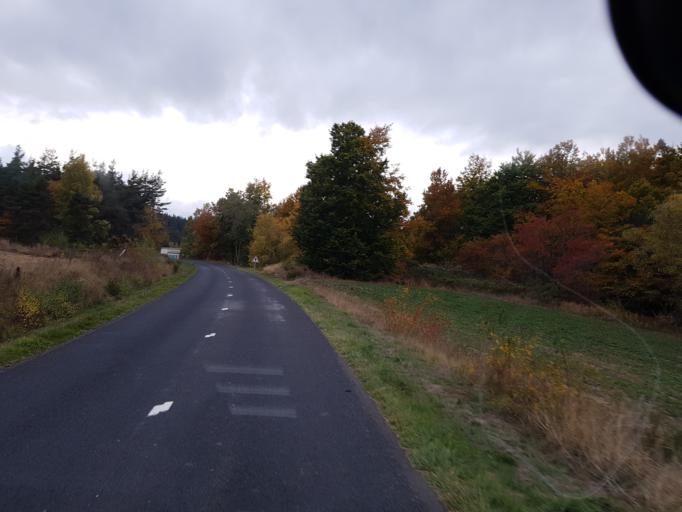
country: FR
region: Languedoc-Roussillon
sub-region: Departement de la Lozere
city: Langogne
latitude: 44.7222
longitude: 3.7652
